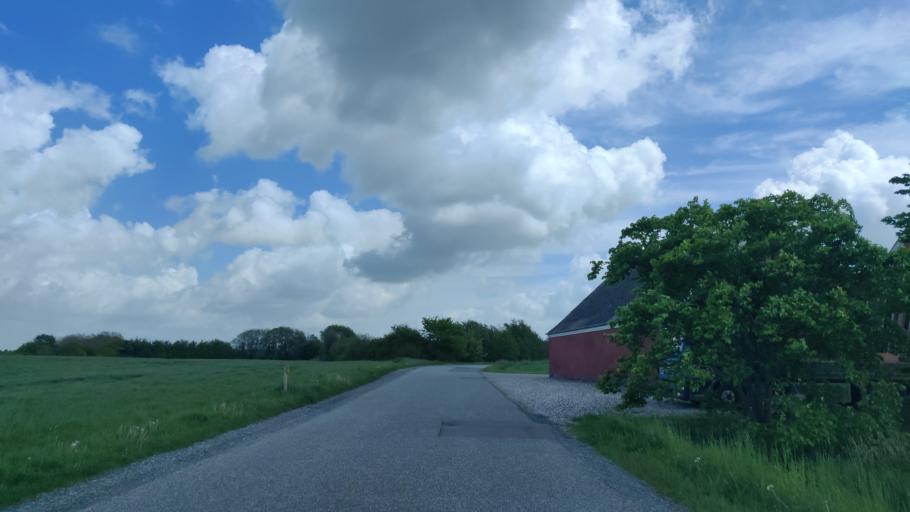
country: DK
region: South Denmark
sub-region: Vejle Kommune
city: Vejle
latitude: 55.6561
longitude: 9.5096
